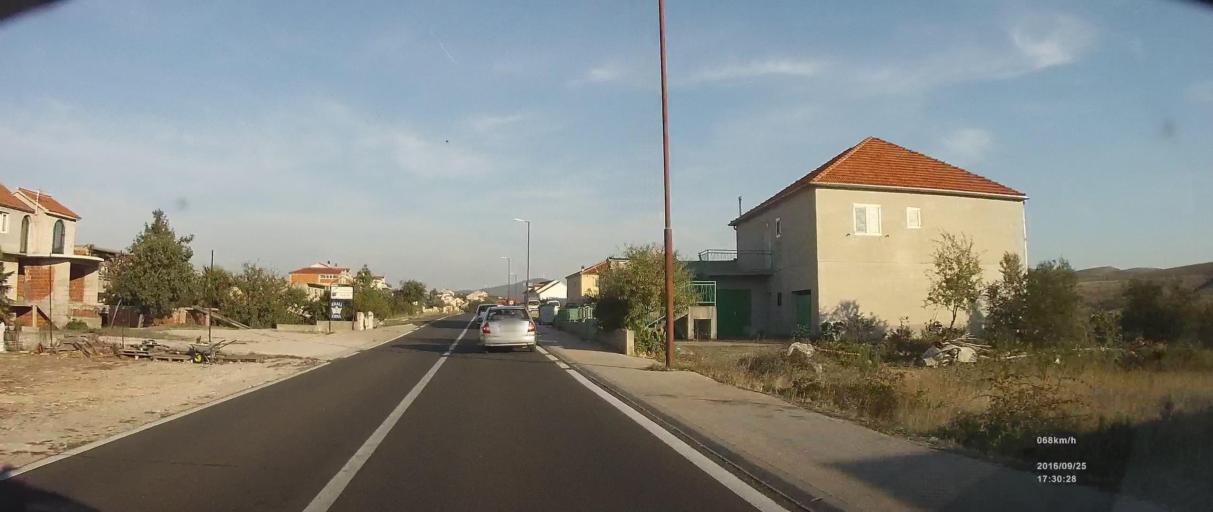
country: HR
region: Sibensko-Kniniska
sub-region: Grad Sibenik
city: Brodarica
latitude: 43.6806
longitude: 15.9780
